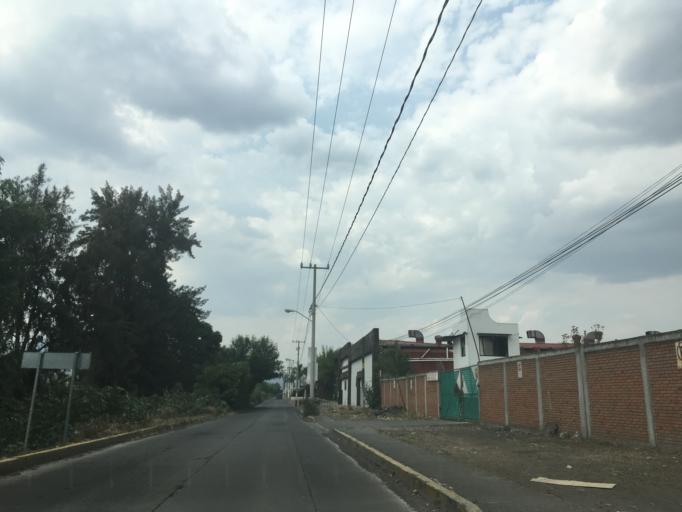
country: MX
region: Michoacan
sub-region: Morelia
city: Morelos
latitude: 19.6760
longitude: -101.2356
